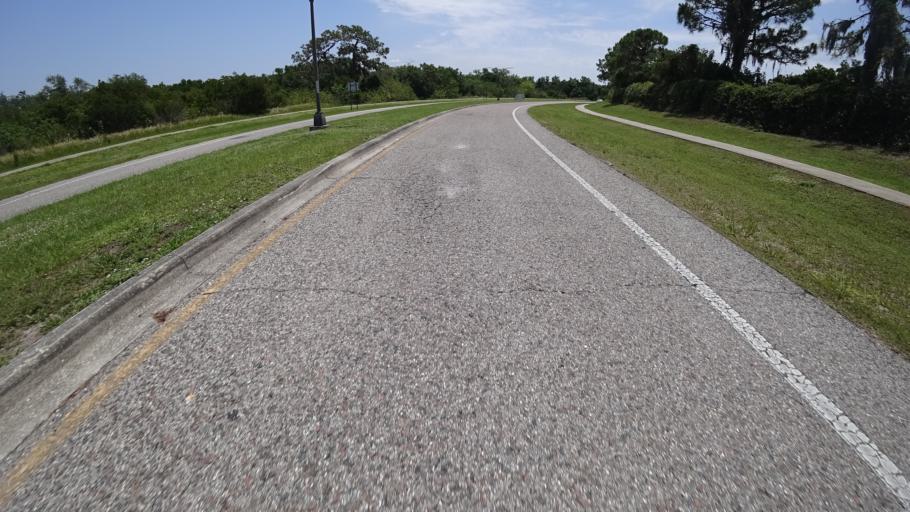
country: US
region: Florida
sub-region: Sarasota County
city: Desoto Lakes
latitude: 27.4140
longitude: -82.4672
